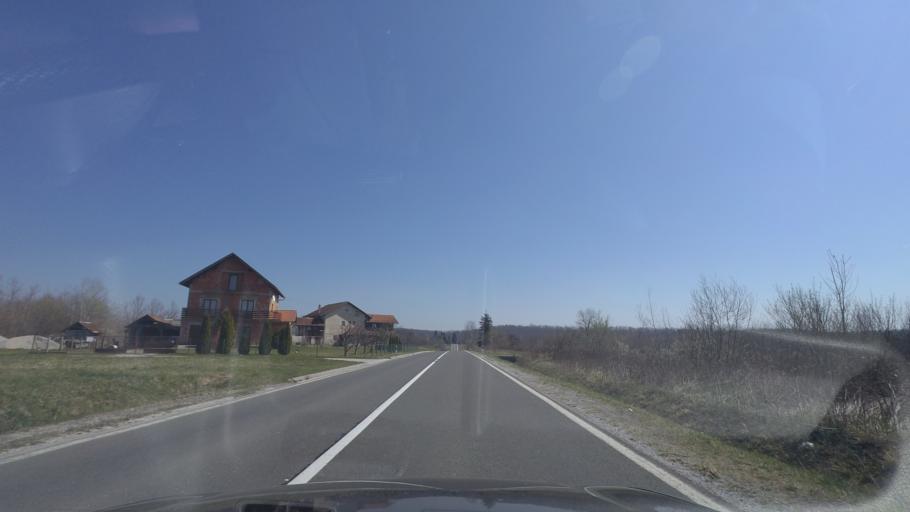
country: HR
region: Sisacko-Moslavacka
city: Gvozd
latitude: 45.3224
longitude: 15.9461
